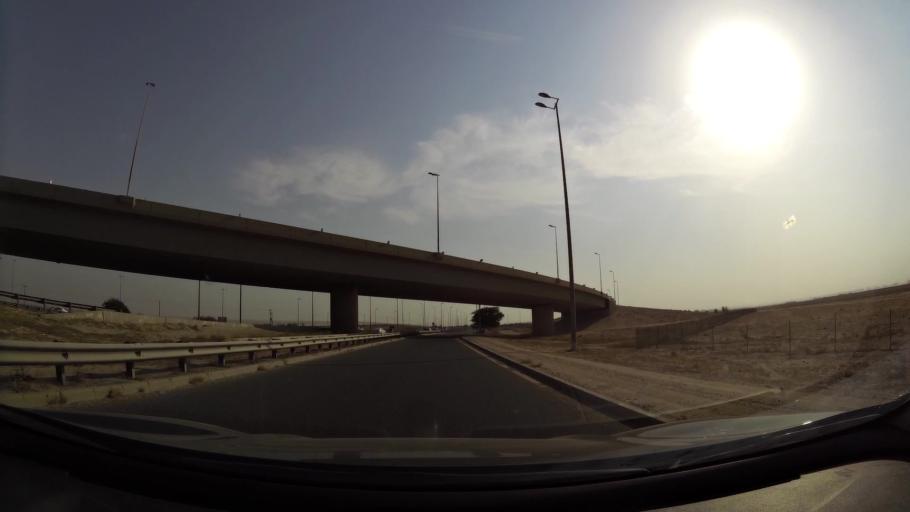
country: KW
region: Mubarak al Kabir
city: Mubarak al Kabir
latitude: 29.1787
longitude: 47.9959
